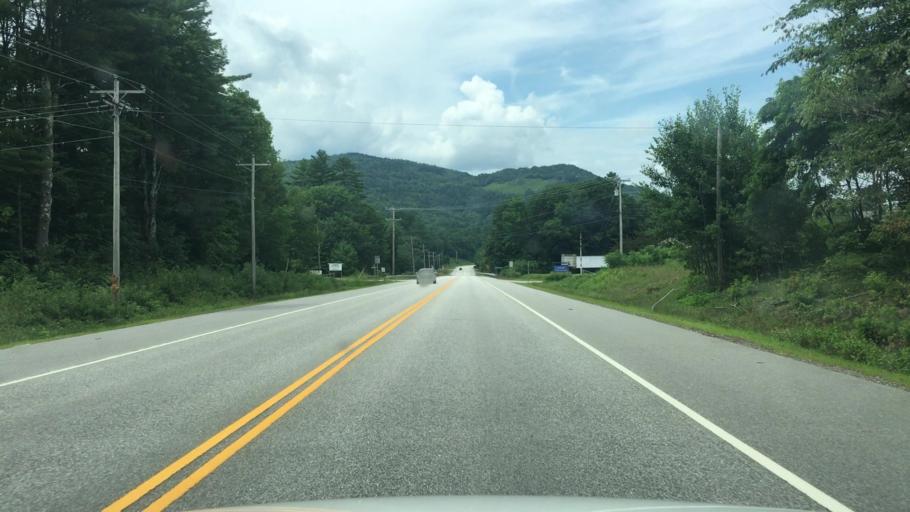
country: US
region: New Hampshire
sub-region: Grafton County
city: Rumney
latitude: 43.7949
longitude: -71.8359
